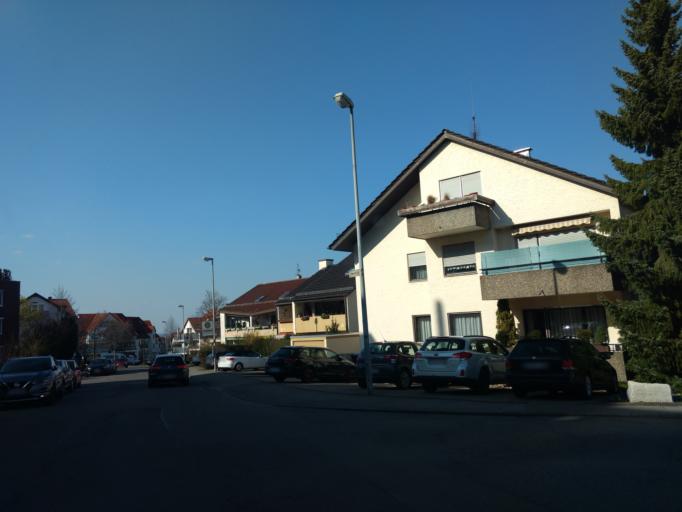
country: DE
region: Baden-Wuerttemberg
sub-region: Regierungsbezirk Stuttgart
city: Filderstadt
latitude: 48.6549
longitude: 9.1909
